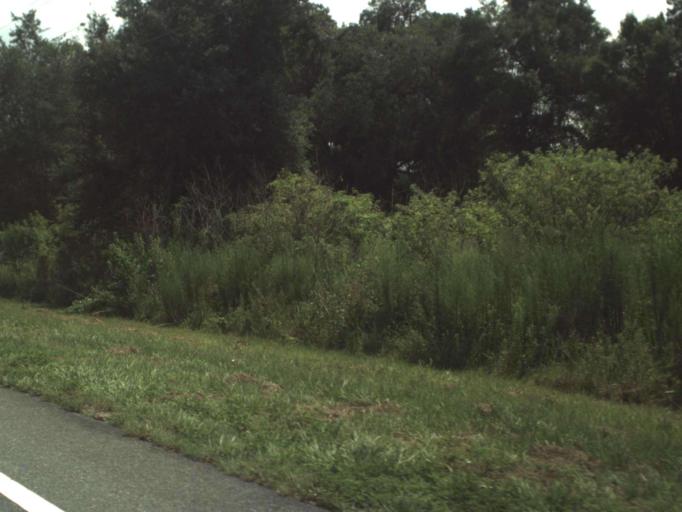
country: US
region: Florida
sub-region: Sumter County
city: Bushnell
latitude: 28.6491
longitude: -82.1193
